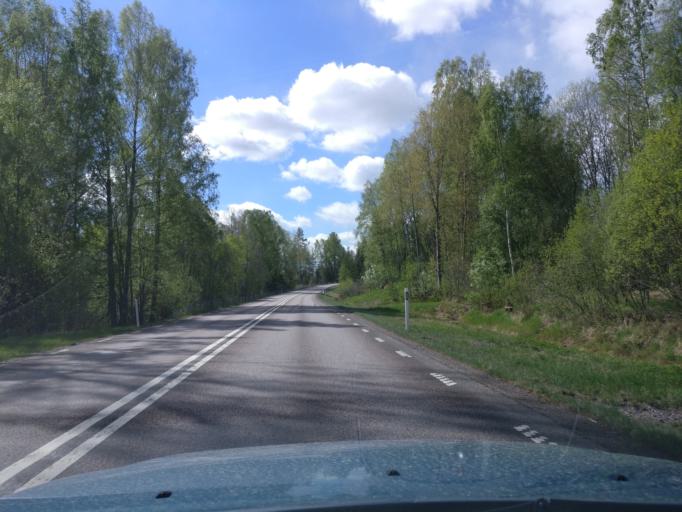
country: SE
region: Vaermland
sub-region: Karlstads Kommun
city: Molkom
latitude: 59.5479
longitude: 13.6517
